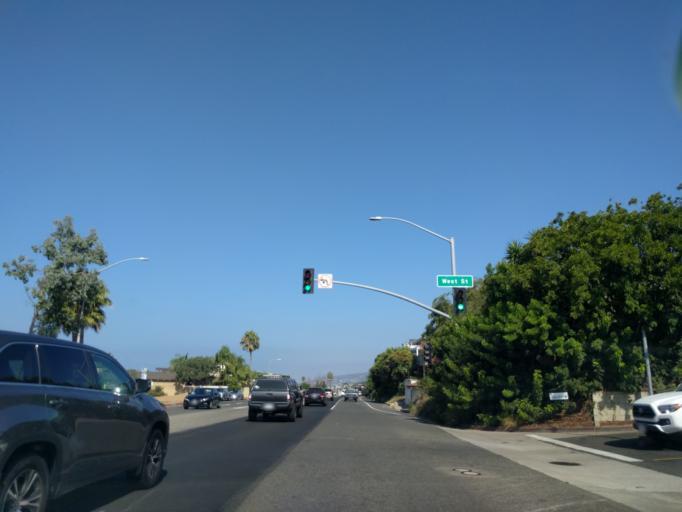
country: US
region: California
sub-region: Orange County
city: Laguna Niguel
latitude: 33.5051
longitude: -117.7465
